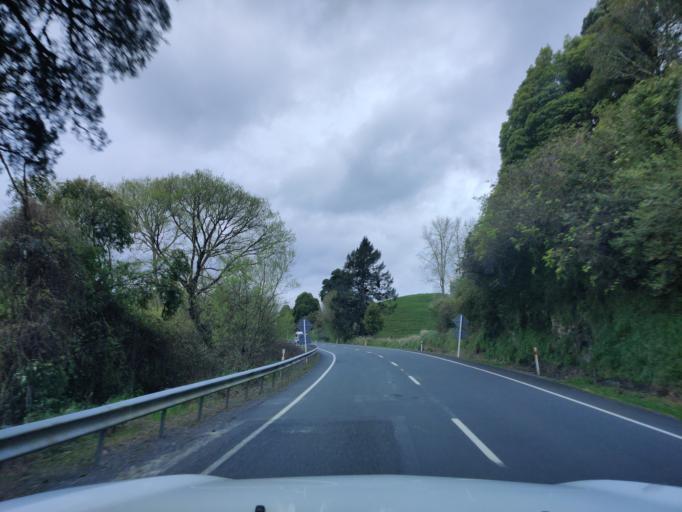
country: NZ
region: Waikato
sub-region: Otorohanga District
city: Otorohanga
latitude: -38.4819
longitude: 175.1748
